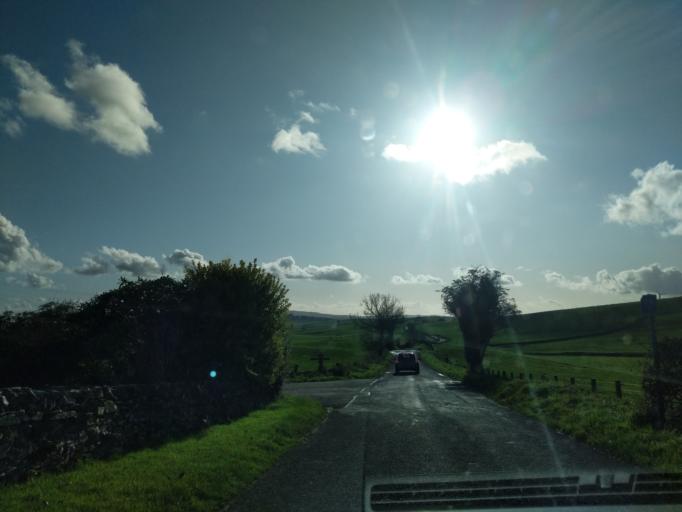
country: GB
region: Scotland
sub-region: Dumfries and Galloway
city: Dalbeattie
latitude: 55.0043
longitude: -3.8172
